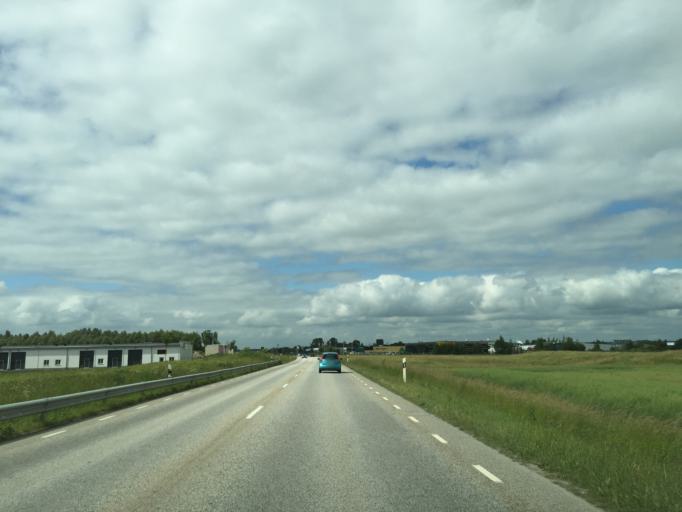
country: SE
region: Skane
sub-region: Staffanstorps Kommun
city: Staffanstorp
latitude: 55.6475
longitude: 13.2294
